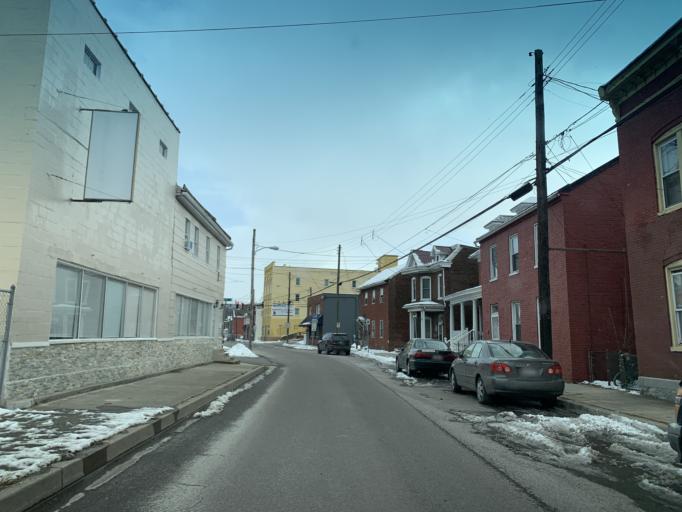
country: US
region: Maryland
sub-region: Allegany County
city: Cumberland
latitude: 39.6570
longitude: -78.7708
